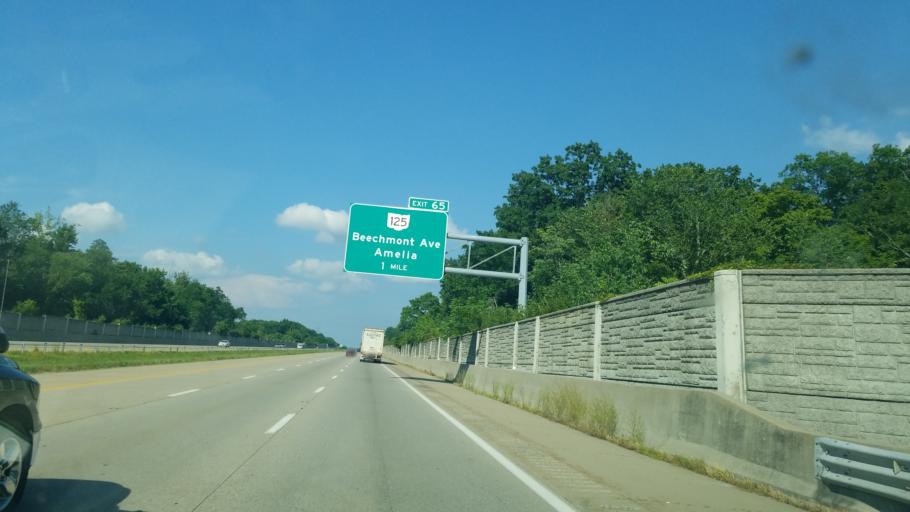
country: US
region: Ohio
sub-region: Hamilton County
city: Cherry Grove
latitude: 39.0583
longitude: -84.3203
